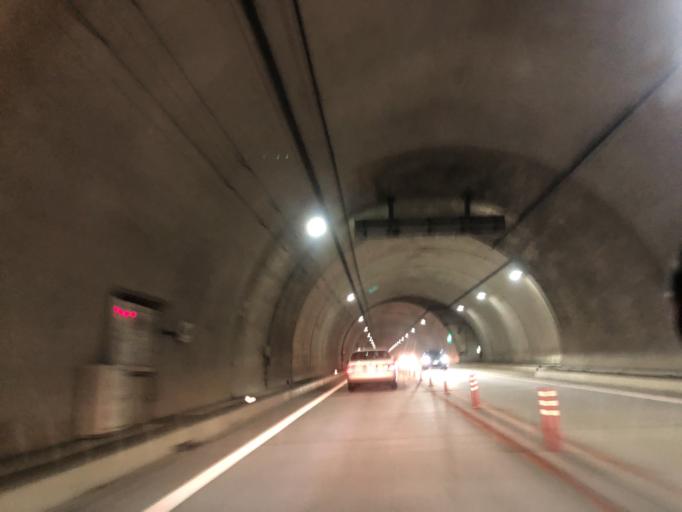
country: JP
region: Fukushima
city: Fukushima-shi
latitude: 37.8095
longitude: 140.4065
